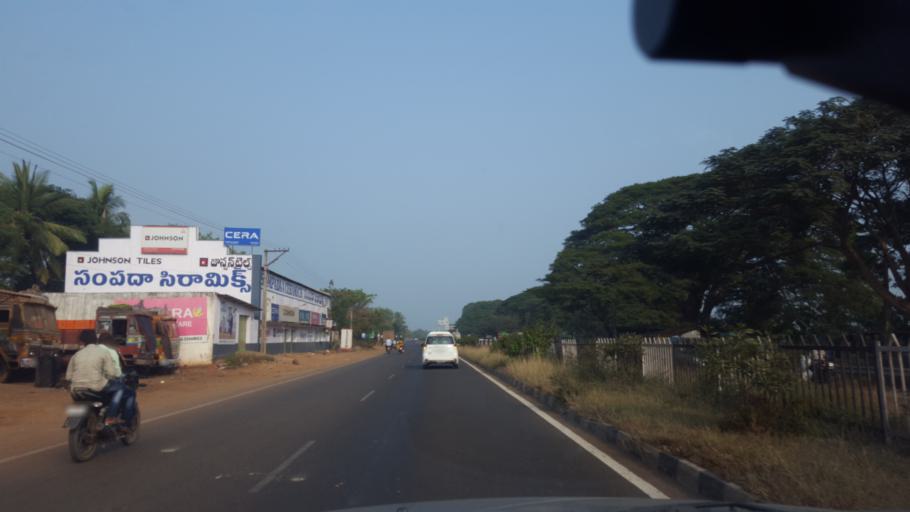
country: IN
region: Andhra Pradesh
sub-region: West Godavari
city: Tadepallegudem
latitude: 16.8212
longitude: 81.4078
